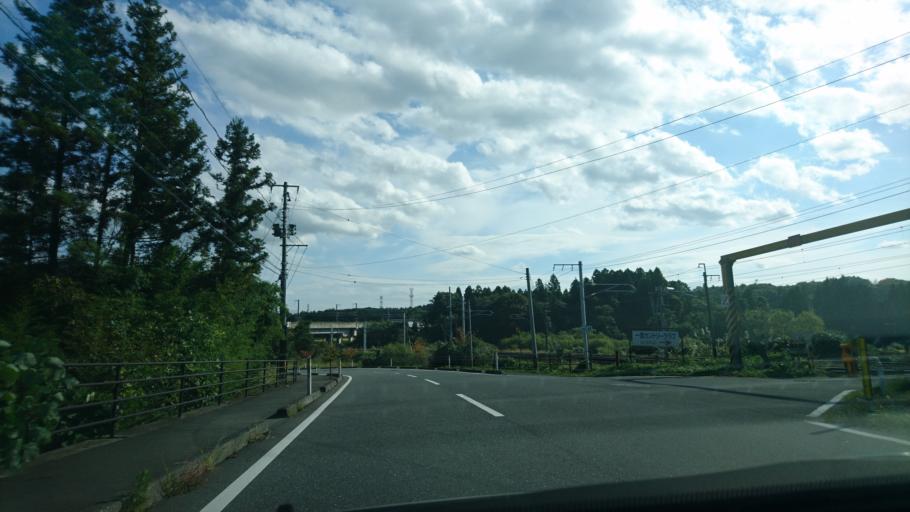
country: JP
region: Iwate
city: Ichinoseki
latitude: 38.8713
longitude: 141.1166
